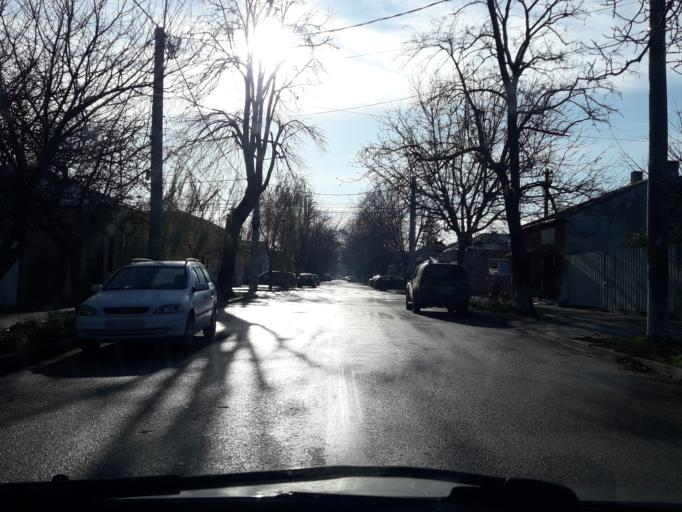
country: RO
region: Galati
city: Galati
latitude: 45.4570
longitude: 28.0378
